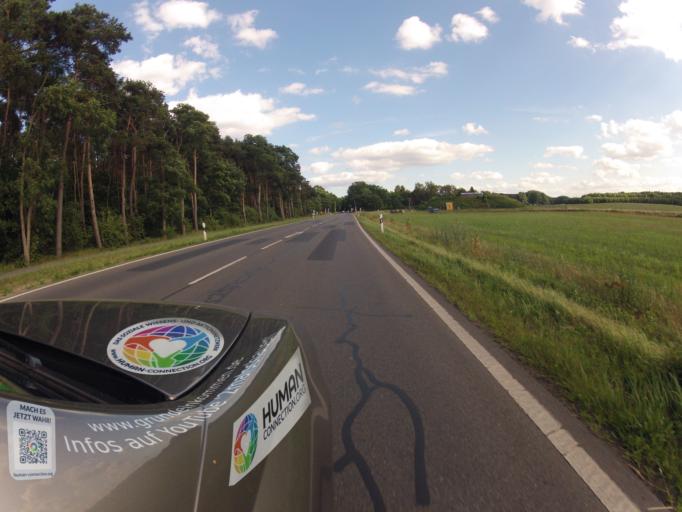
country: DE
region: Mecklenburg-Vorpommern
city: Koserow
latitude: 54.0422
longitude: 14.0088
